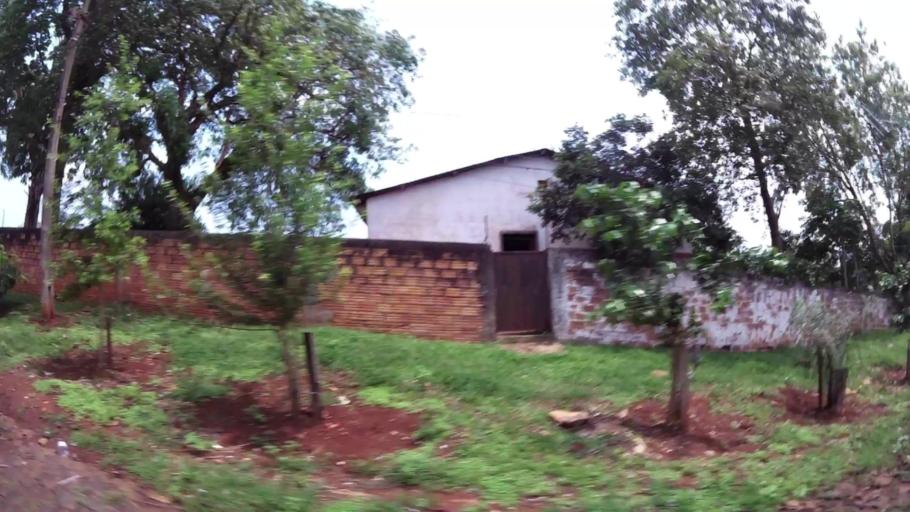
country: PY
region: Alto Parana
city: Ciudad del Este
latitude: -25.5056
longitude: -54.6175
